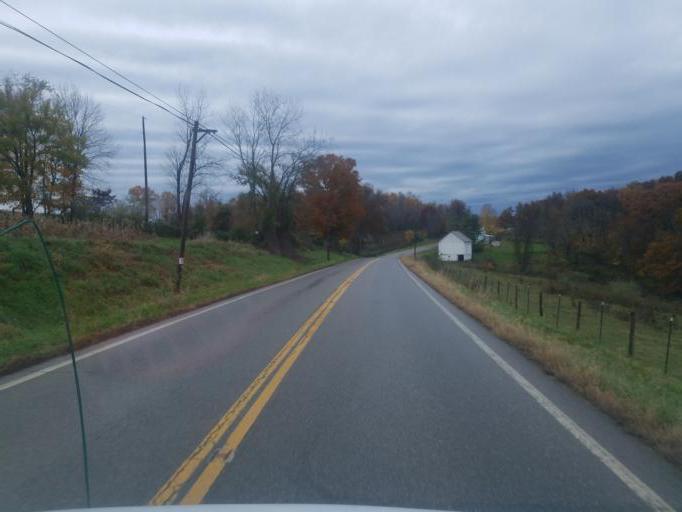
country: US
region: Ohio
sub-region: Morgan County
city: McConnelsville
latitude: 39.5191
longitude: -81.8506
